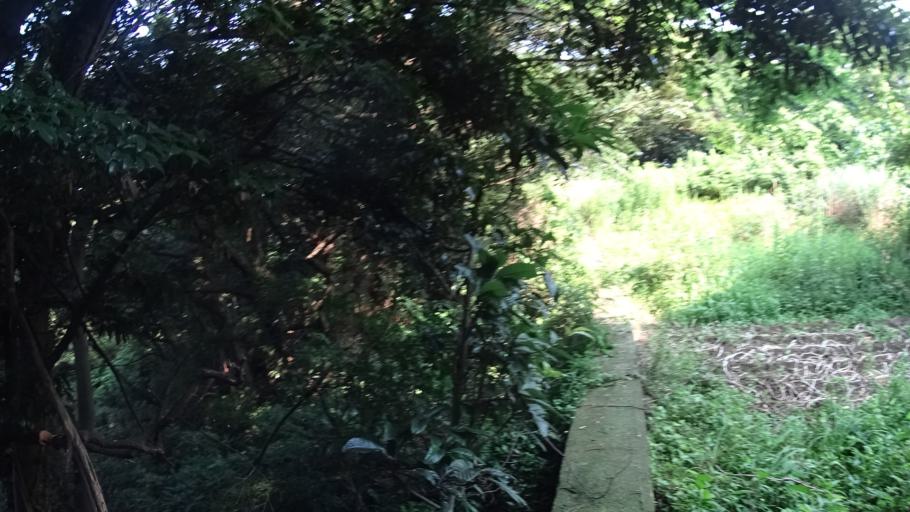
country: JP
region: Kanagawa
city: Zushi
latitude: 35.3047
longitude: 139.6224
